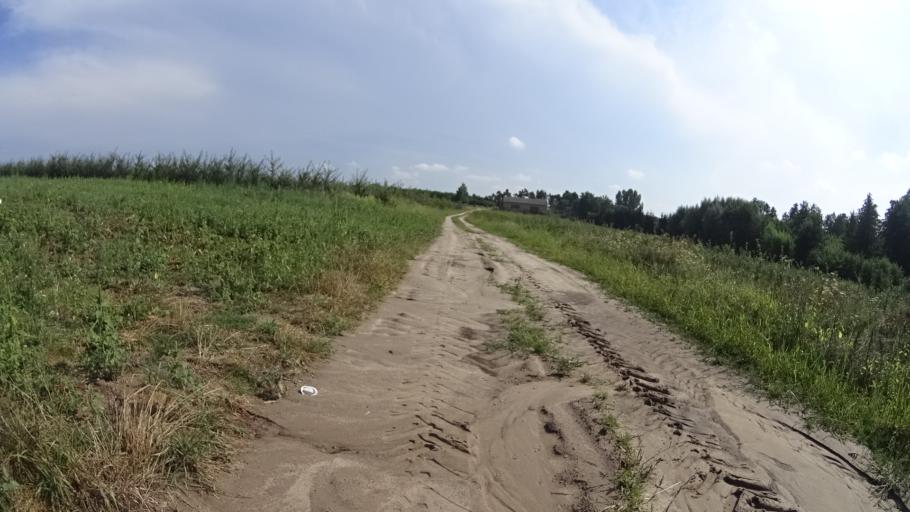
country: PL
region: Masovian Voivodeship
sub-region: Powiat grojecki
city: Goszczyn
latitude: 51.6887
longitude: 20.8399
